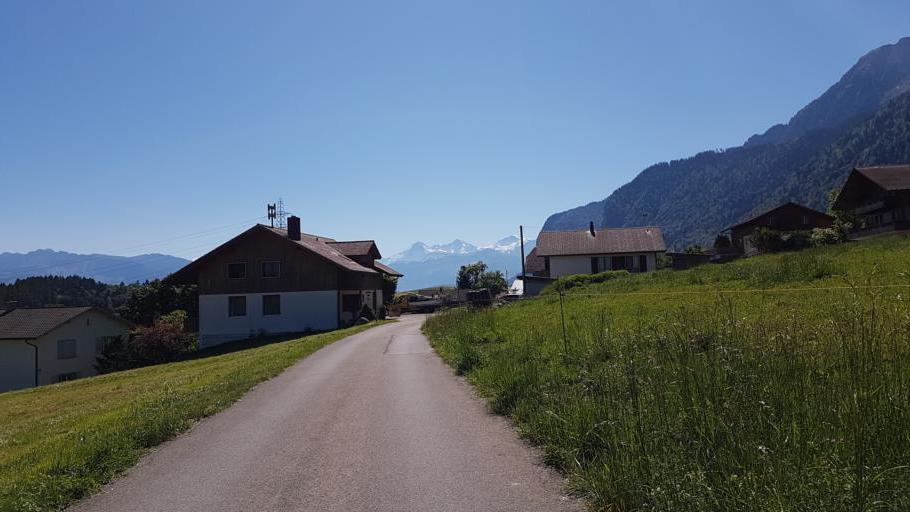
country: CH
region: Bern
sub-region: Thun District
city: Blumenstein
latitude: 46.7237
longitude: 7.5379
